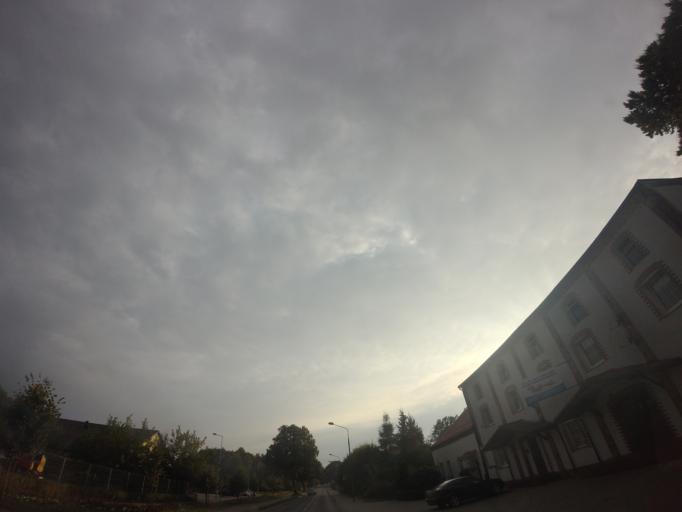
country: PL
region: West Pomeranian Voivodeship
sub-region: Powiat drawski
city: Kalisz Pomorski
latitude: 53.2917
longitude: 15.9000
